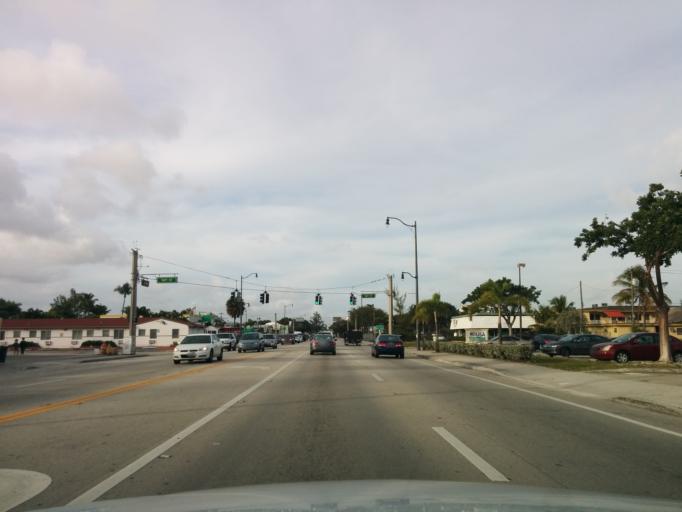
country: US
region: Florida
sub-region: Broward County
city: Hollywood
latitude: 26.0256
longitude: -80.1432
